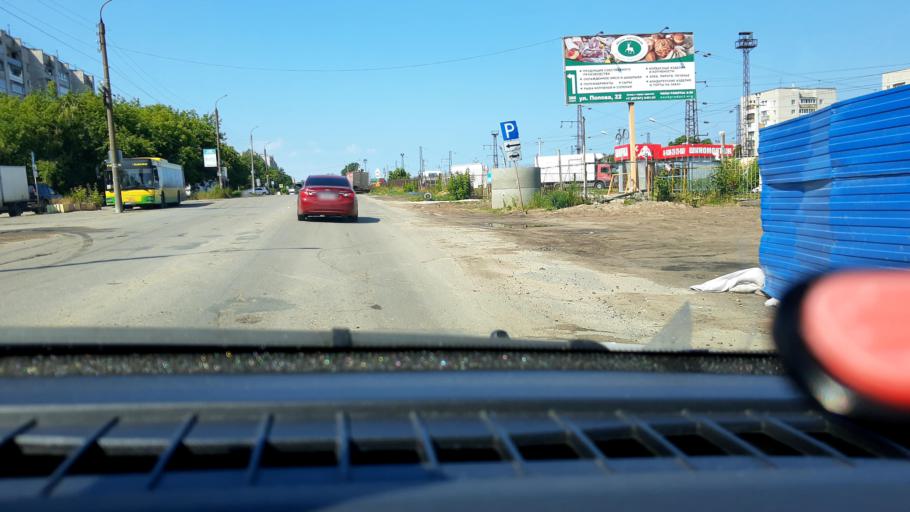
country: RU
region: Nizjnij Novgorod
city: Dzerzhinsk
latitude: 56.2334
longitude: 43.4844
